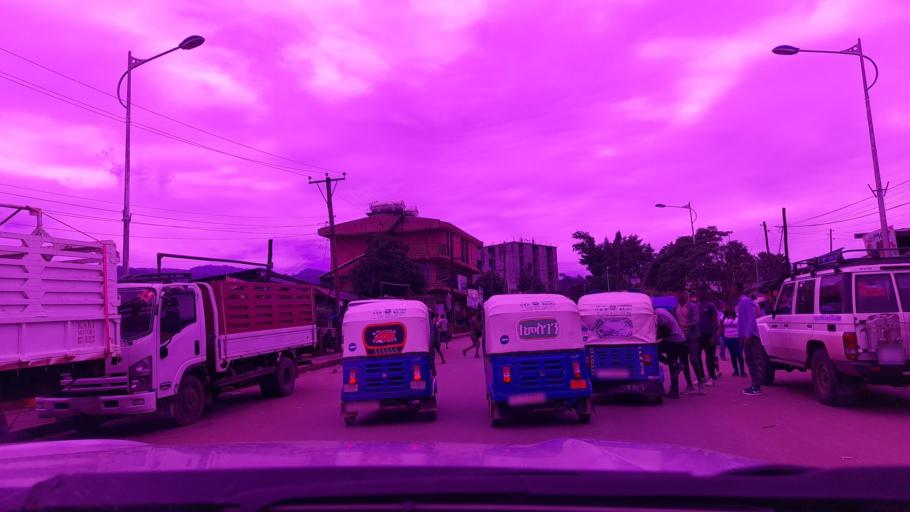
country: ET
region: Southern Nations, Nationalities, and People's Region
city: Mizan Teferi
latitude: 6.9947
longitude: 35.5940
